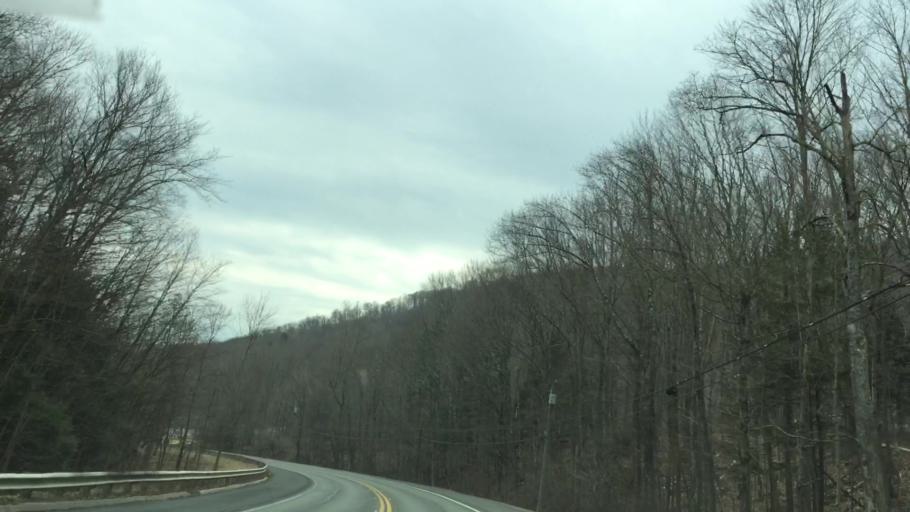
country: US
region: Massachusetts
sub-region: Berkshire County
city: Williamstown
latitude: 42.6250
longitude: -73.2309
